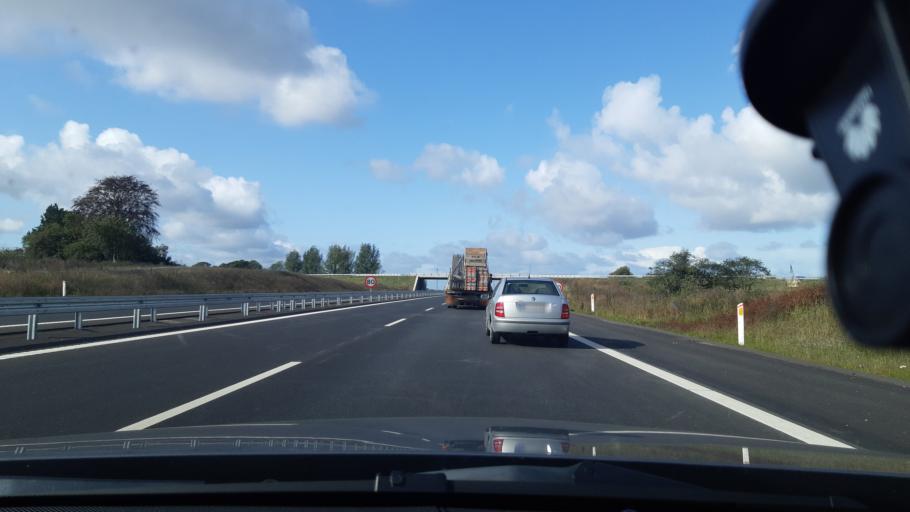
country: DK
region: Zealand
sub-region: Holbaek Kommune
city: Holbaek
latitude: 55.6592
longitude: 11.6213
